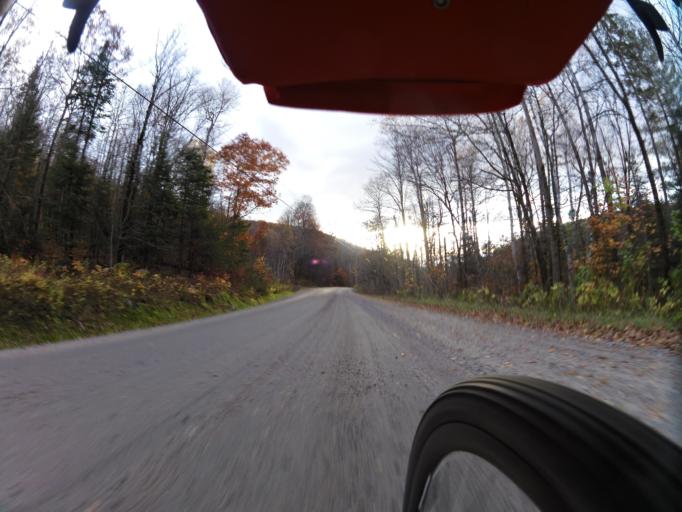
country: CA
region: Quebec
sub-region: Outaouais
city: Shawville
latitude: 45.6784
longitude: -76.2675
